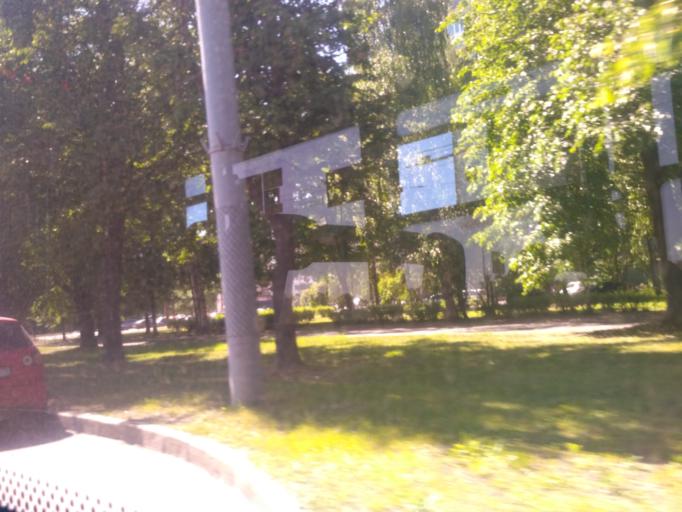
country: RU
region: Leningrad
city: Kalininskiy
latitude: 59.9650
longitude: 30.4176
